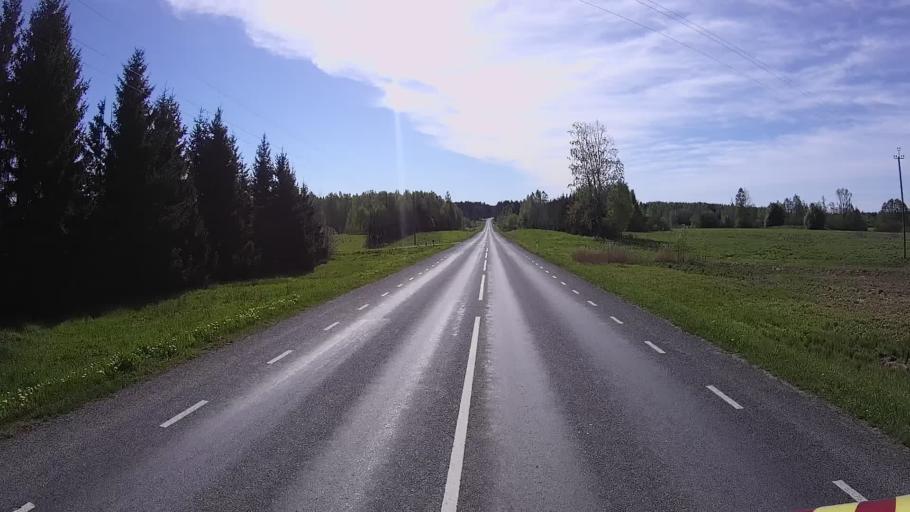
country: EE
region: Polvamaa
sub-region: Polva linn
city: Polva
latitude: 58.1885
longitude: 27.0917
